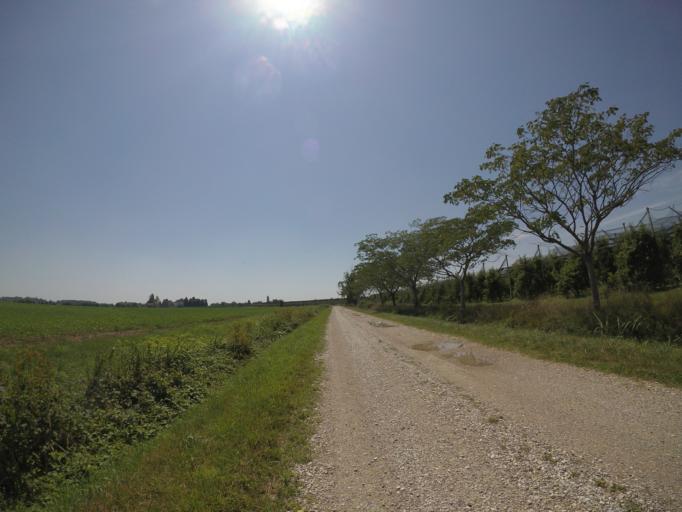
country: IT
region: Friuli Venezia Giulia
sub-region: Provincia di Udine
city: Varmo
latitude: 45.9156
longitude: 13.0024
